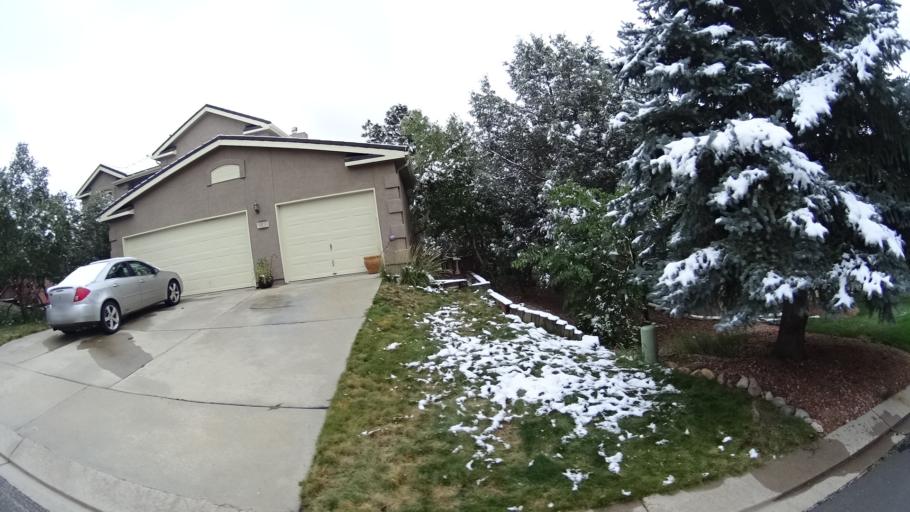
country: US
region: Colorado
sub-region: El Paso County
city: Colorado Springs
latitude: 38.9171
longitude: -104.7992
